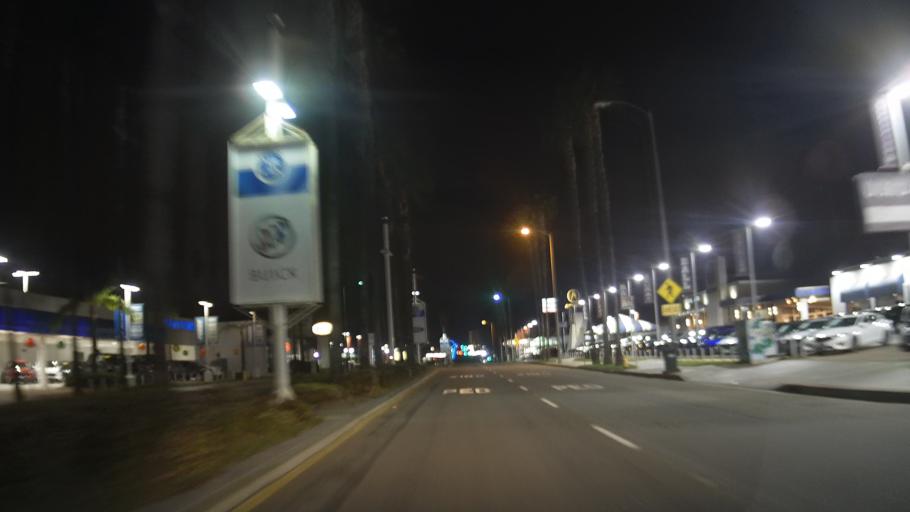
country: US
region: California
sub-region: San Diego County
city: National City
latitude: 32.6645
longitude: -117.1024
